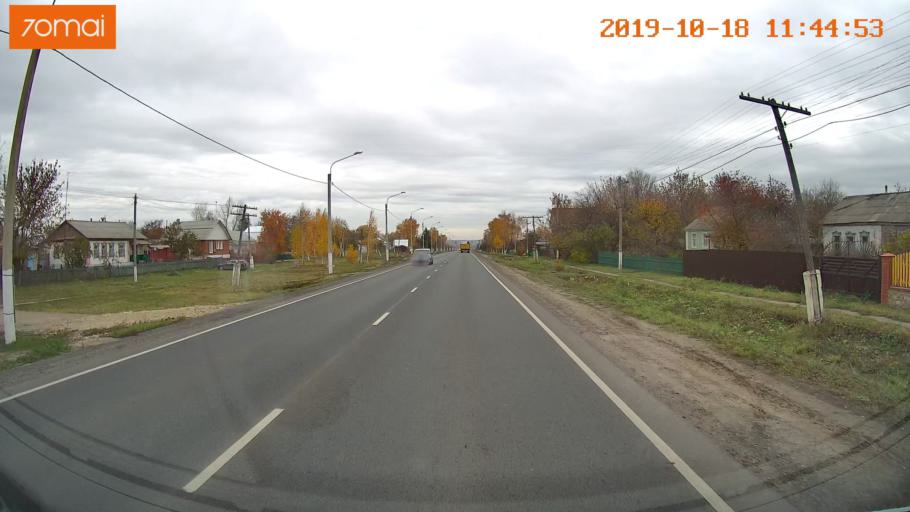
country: RU
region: Rjazan
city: Mikhaylov
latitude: 54.2059
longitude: 38.9633
